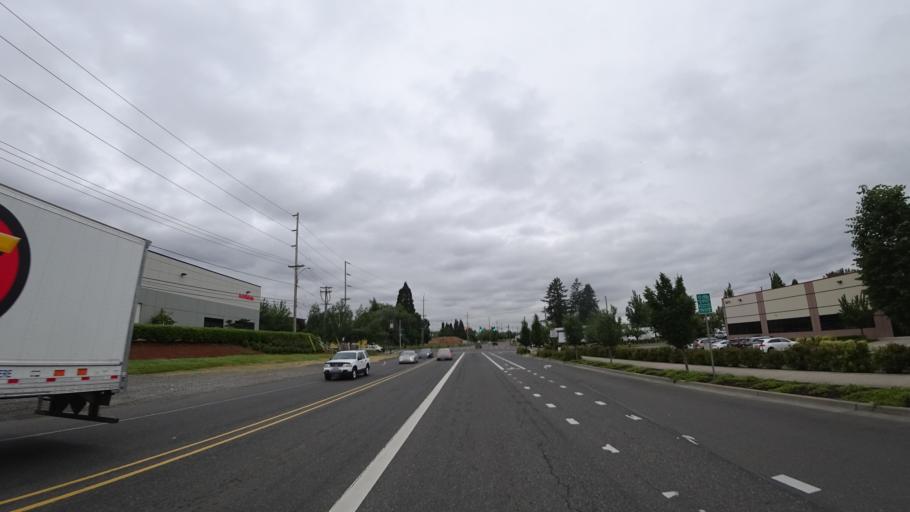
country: US
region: Oregon
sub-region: Multnomah County
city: Fairview
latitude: 45.5459
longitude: -122.4759
